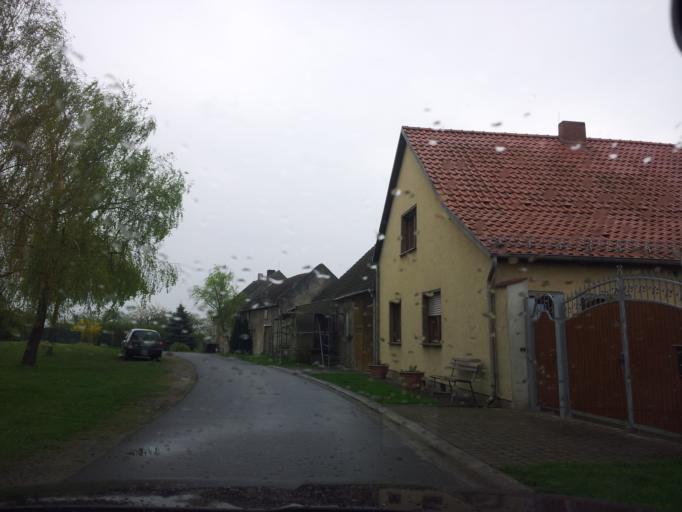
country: DE
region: Saxony-Anhalt
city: Kropstadt
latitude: 52.0124
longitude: 12.7901
